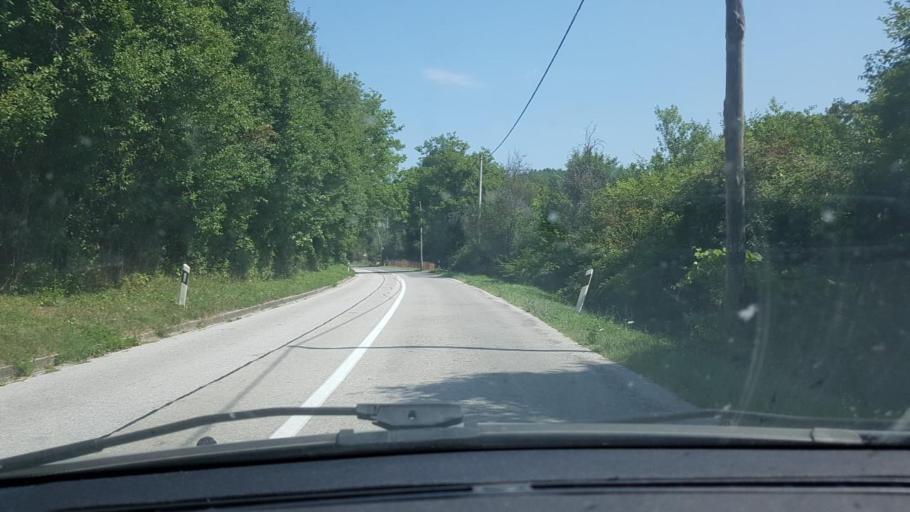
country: BA
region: Federation of Bosnia and Herzegovina
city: Velika Kladusa
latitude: 45.2293
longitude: 15.7340
